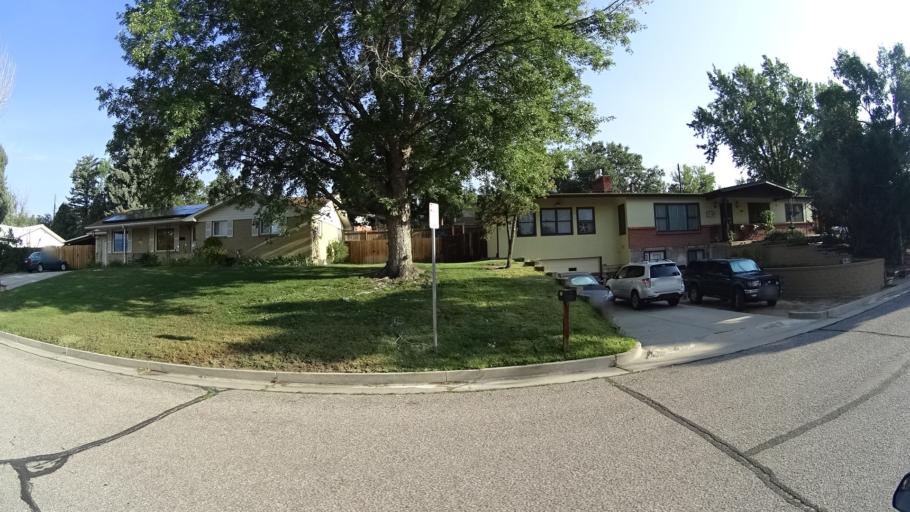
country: US
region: Colorado
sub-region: El Paso County
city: Colorado Springs
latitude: 38.8859
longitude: -104.7959
